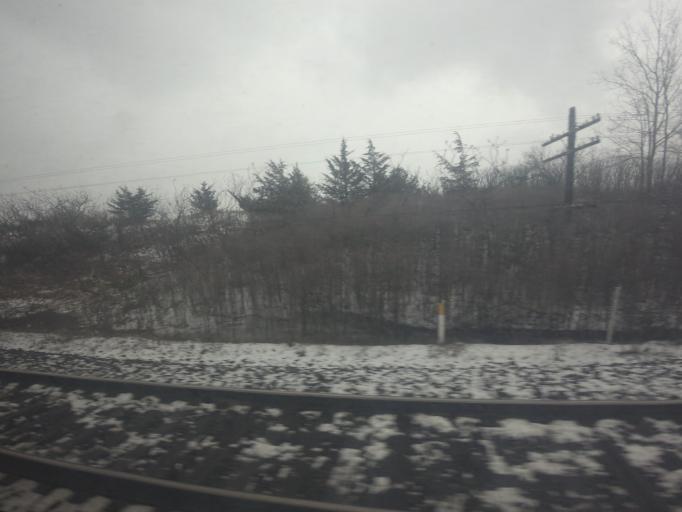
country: CA
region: Ontario
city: Quinte West
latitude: 44.0967
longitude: -77.6205
